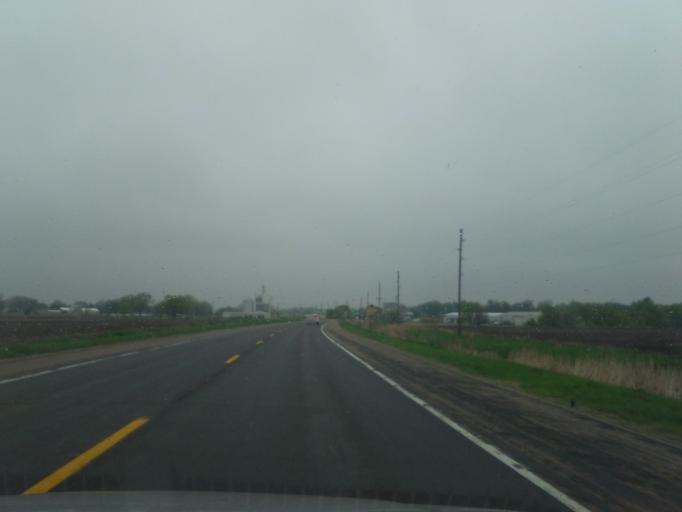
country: US
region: Nebraska
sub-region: Cuming County
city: West Point
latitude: 41.9232
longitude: -96.8030
